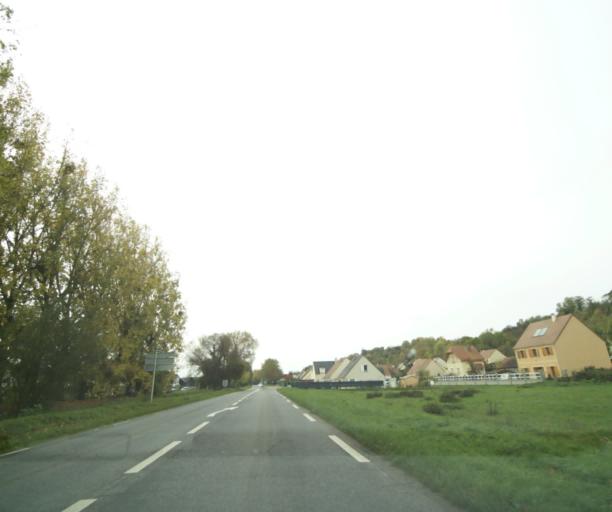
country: FR
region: Centre
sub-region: Departement d'Eure-et-Loir
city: Dreux
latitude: 48.7520
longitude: 1.3896
